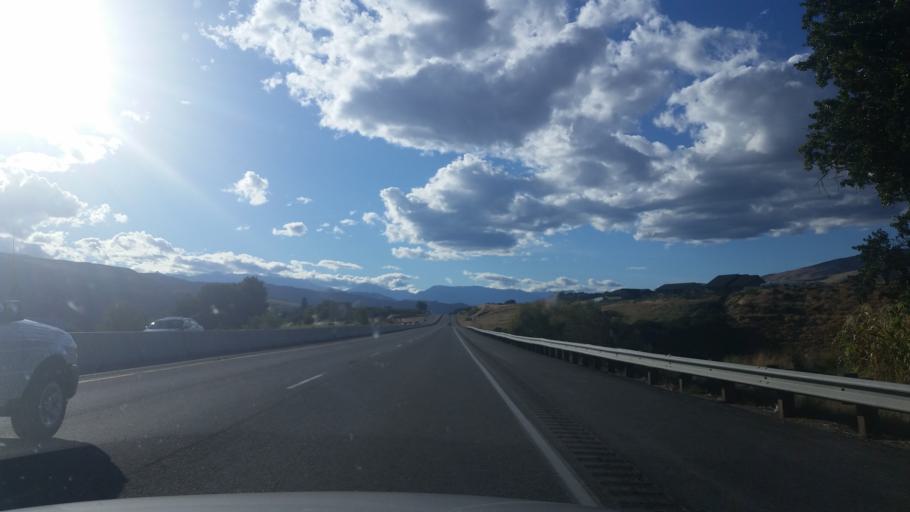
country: US
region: Washington
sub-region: Chelan County
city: Sunnyslope
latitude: 47.4705
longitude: -120.3469
